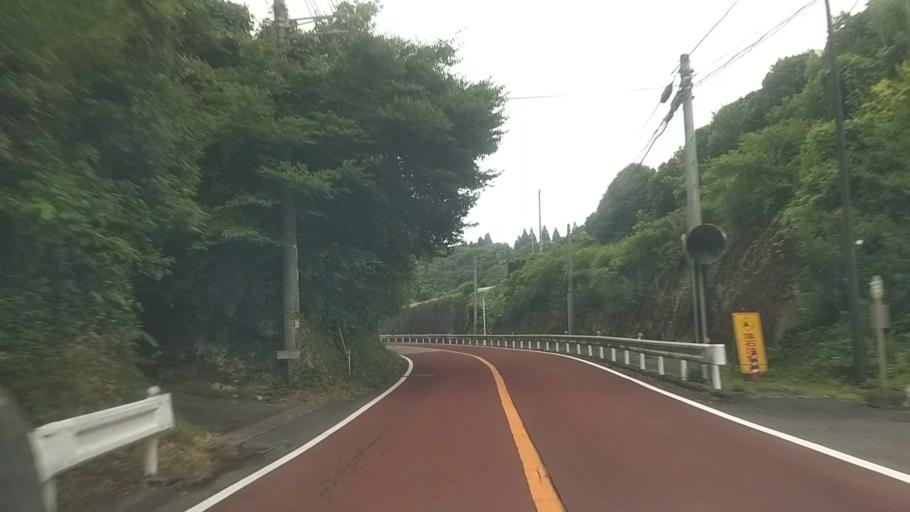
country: JP
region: Chiba
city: Katsuura
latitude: 35.2489
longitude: 140.2122
